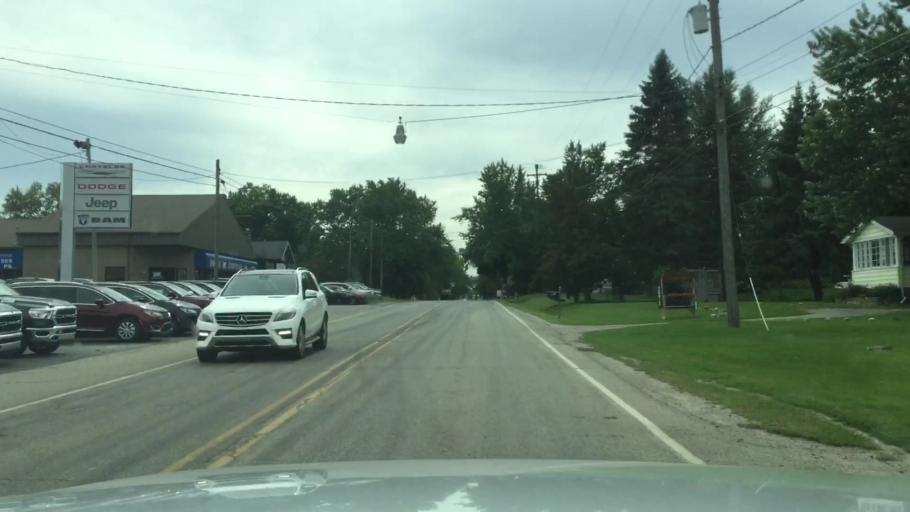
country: US
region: Michigan
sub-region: Shiawassee County
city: Durand
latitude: 42.9201
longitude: -83.9850
